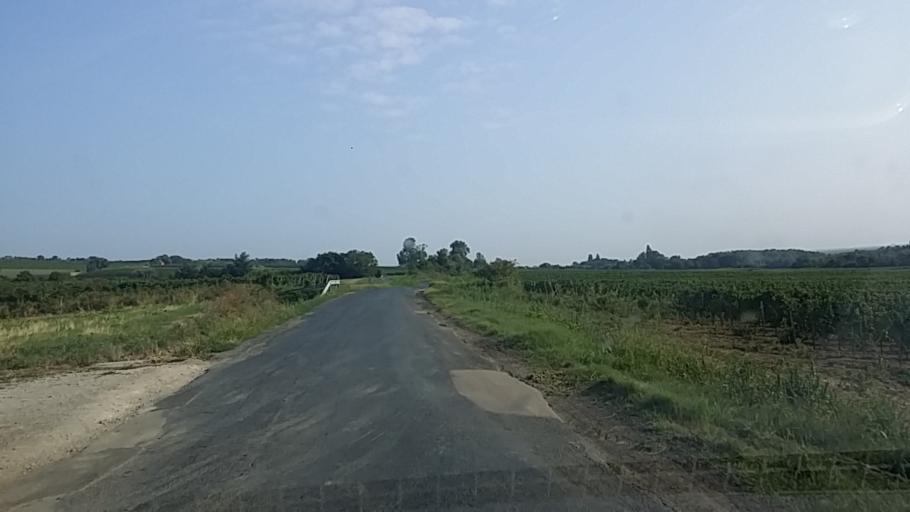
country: HU
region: Gyor-Moson-Sopron
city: Fertorakos
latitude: 47.6627
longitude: 16.6685
